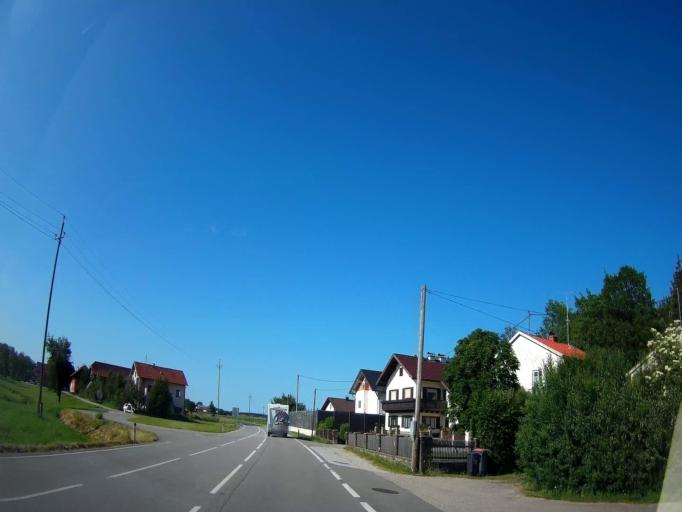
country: AT
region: Upper Austria
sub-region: Politischer Bezirk Braunau am Inn
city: Braunau am Inn
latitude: 48.1637
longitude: 13.0496
